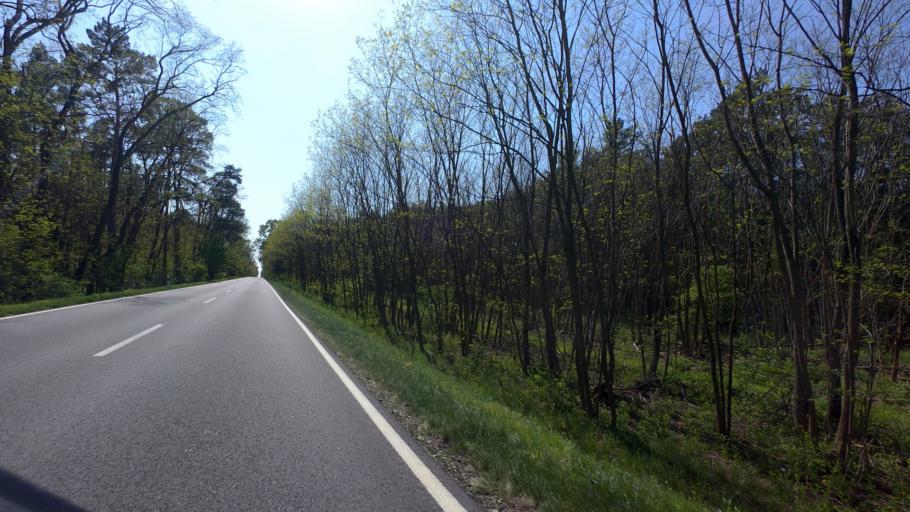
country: DE
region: Brandenburg
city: Tauche
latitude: 52.0487
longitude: 14.1214
